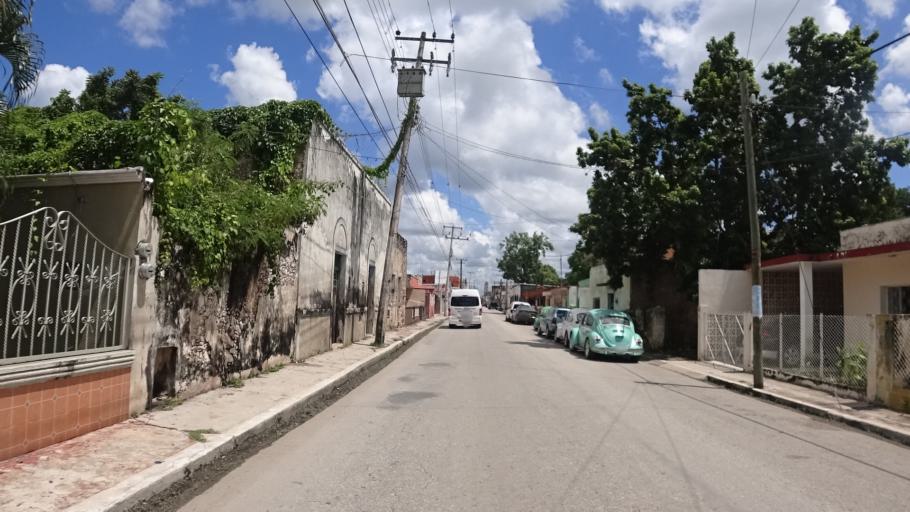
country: MX
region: Yucatan
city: Valladolid
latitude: 20.6899
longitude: -88.2095
